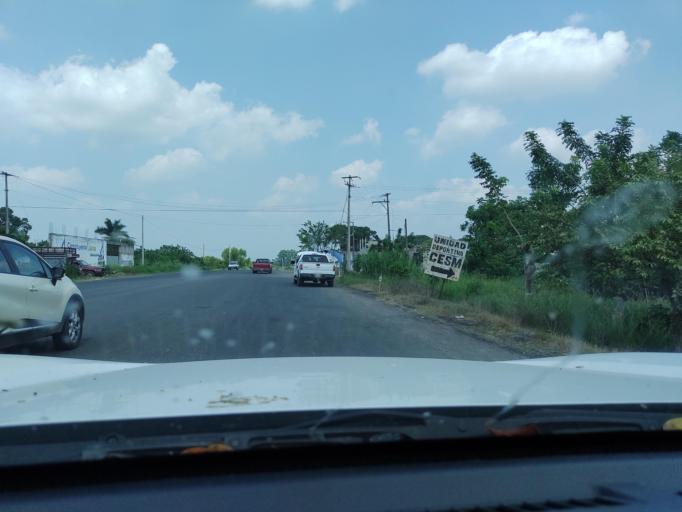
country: MX
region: Veracruz
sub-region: Atzalan
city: Colonias Pedernales
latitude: 20.0596
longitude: -97.0309
